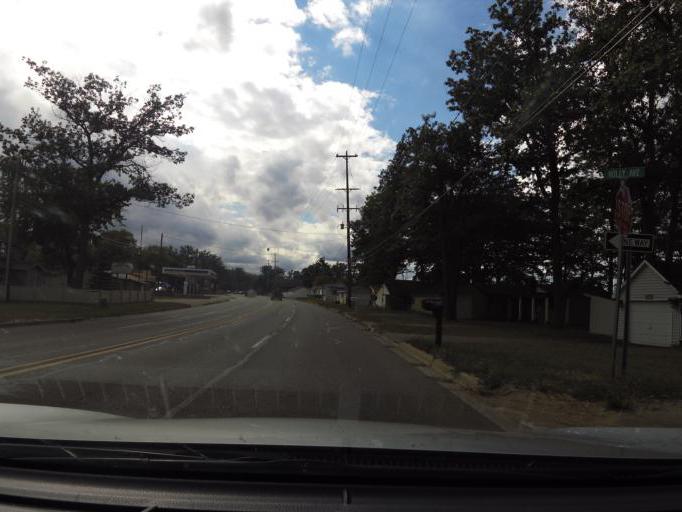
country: US
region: Michigan
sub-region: Roscommon County
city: Prudenville
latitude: 44.3035
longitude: -84.6434
